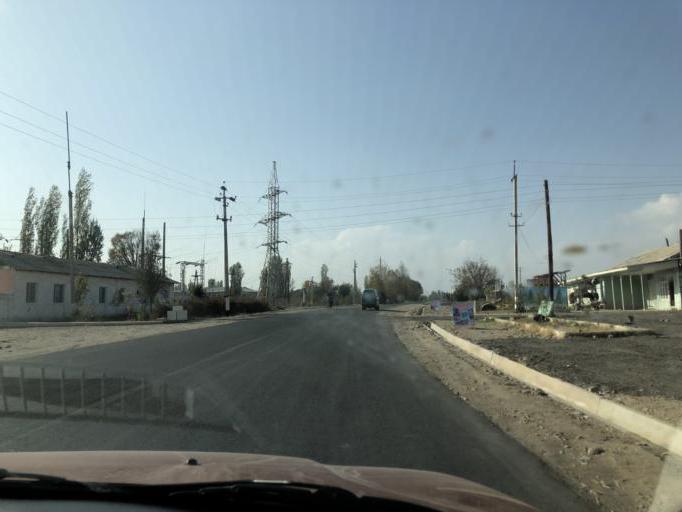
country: UZ
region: Namangan
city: Chust Shahri
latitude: 41.0742
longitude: 71.2003
